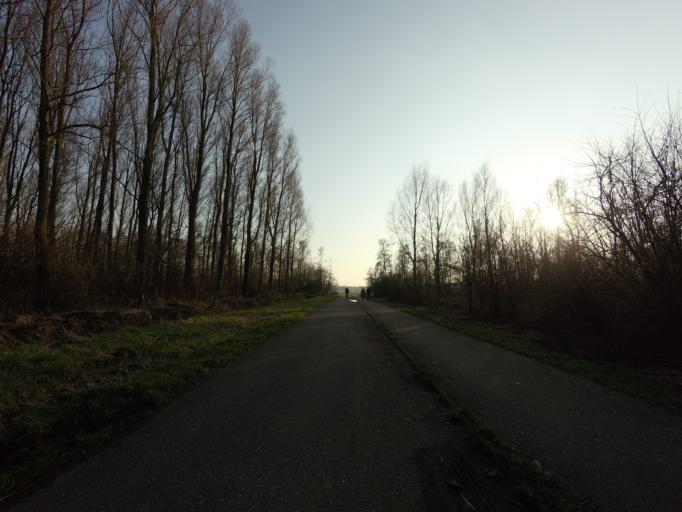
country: NL
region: North Holland
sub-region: Gemeente Haarlem
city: Haarlem
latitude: 52.3625
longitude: 4.6711
